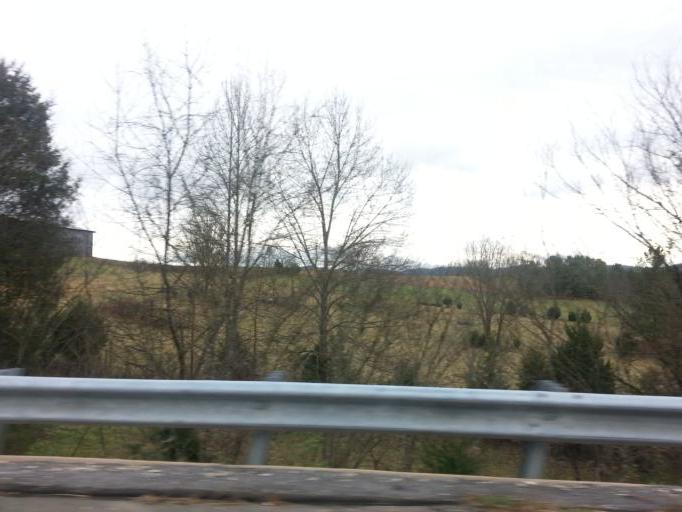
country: US
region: Tennessee
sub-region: Greene County
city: Mosheim
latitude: 36.0546
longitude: -82.9825
